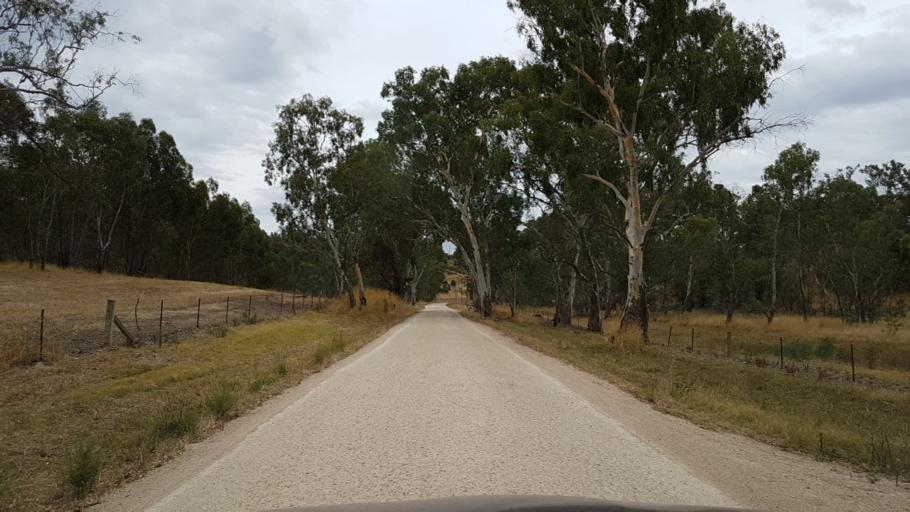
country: AU
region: South Australia
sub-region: Adelaide Hills
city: Gumeracha
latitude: -34.8090
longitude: 138.8353
